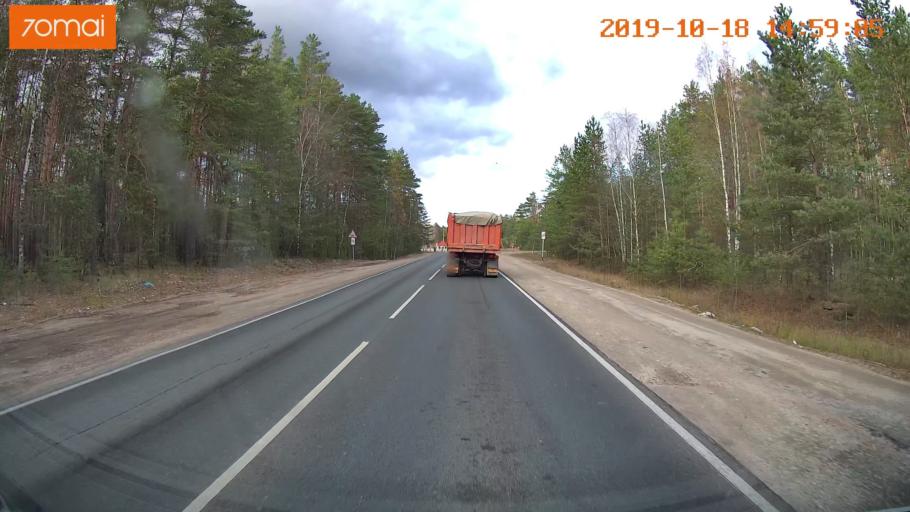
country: RU
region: Vladimir
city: Kurlovo
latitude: 55.4964
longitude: 40.5747
